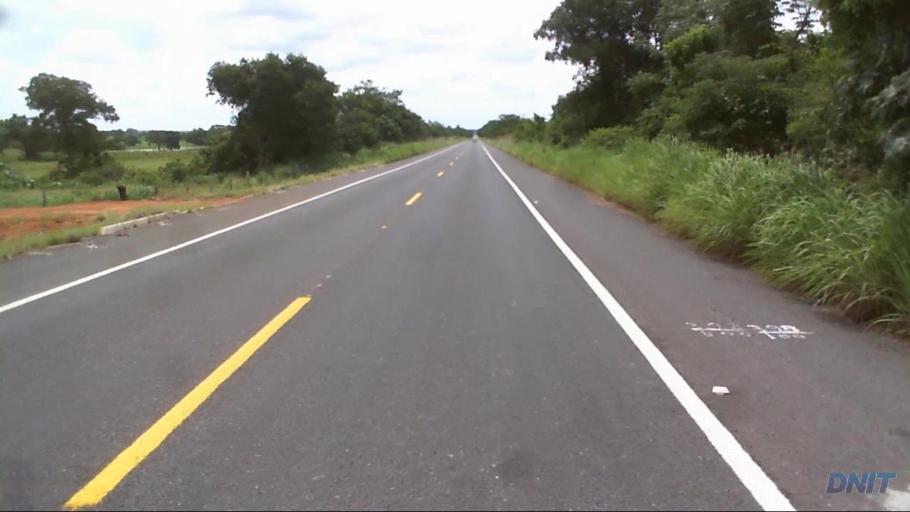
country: BR
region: Goias
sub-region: Sao Miguel Do Araguaia
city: Sao Miguel do Araguaia
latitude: -13.2876
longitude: -50.4581
